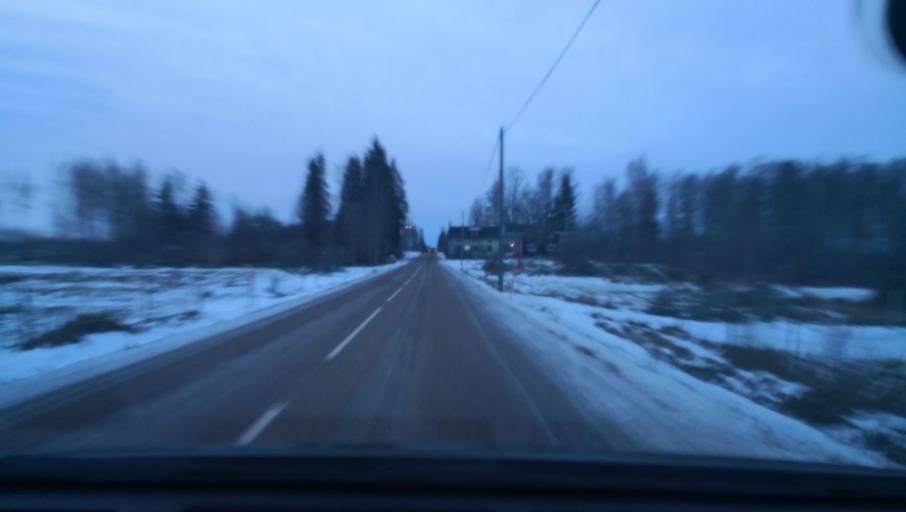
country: SE
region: Dalarna
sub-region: Avesta Kommun
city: Horndal
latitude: 60.1901
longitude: 16.4694
